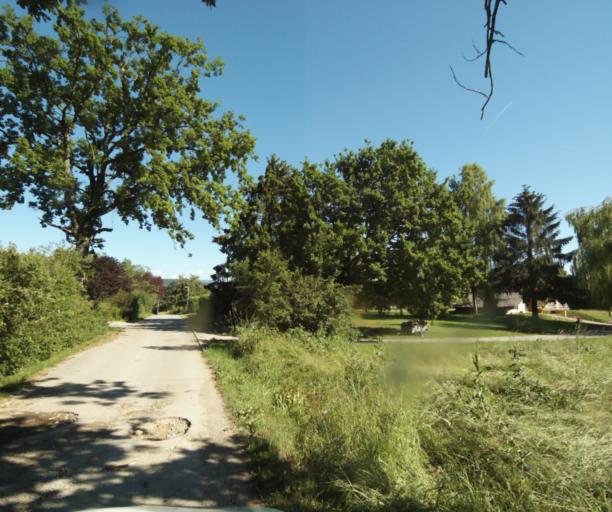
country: FR
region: Rhone-Alpes
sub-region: Departement de la Haute-Savoie
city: Messery
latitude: 46.3335
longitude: 6.2995
